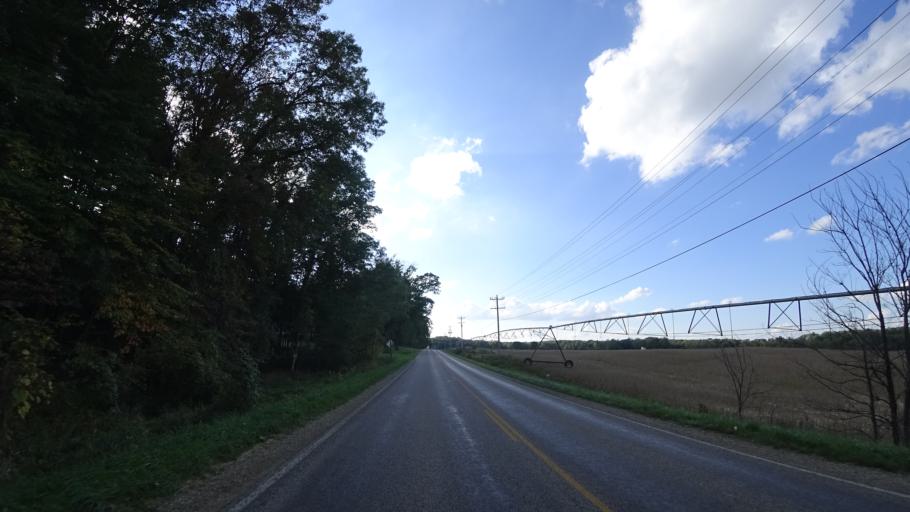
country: US
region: Michigan
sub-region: Saint Joseph County
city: Sturgis
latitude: 41.8538
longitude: -85.4606
